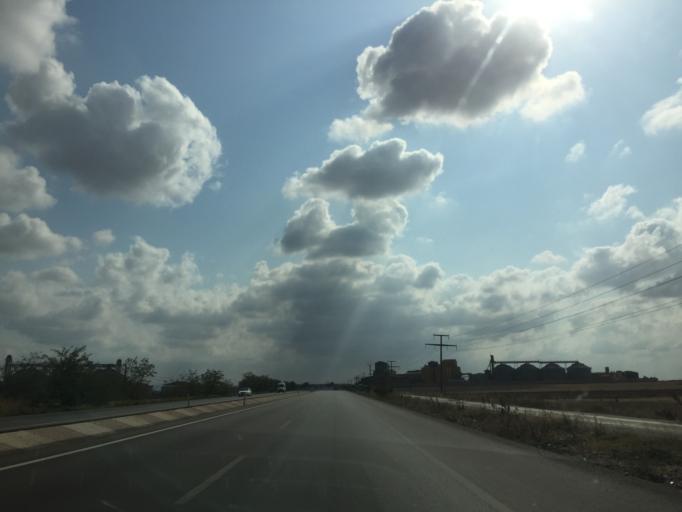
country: TR
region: Balikesir
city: Edincik
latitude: 40.3153
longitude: 27.8446
